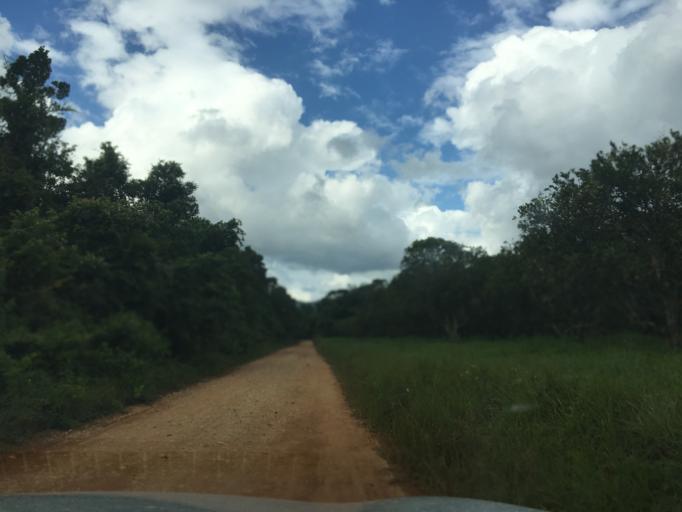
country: BZ
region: Stann Creek
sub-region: Dangriga
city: Dangriga
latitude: 16.9357
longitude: -88.3548
